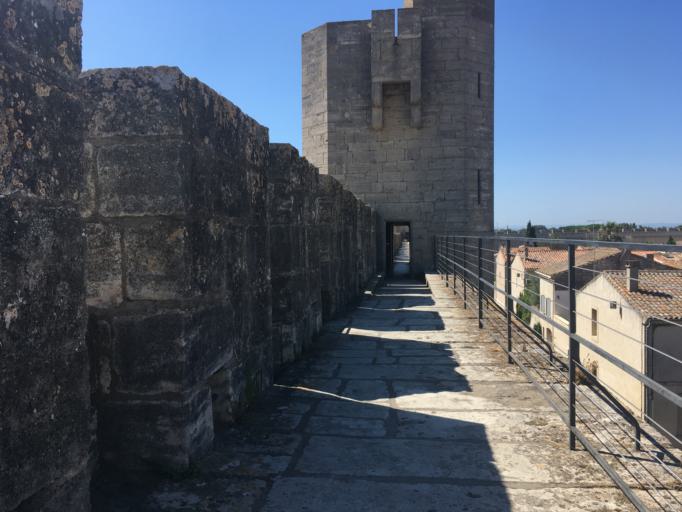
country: FR
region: Languedoc-Roussillon
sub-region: Departement du Gard
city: Aigues-Mortes
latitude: 43.5655
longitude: 4.1891
